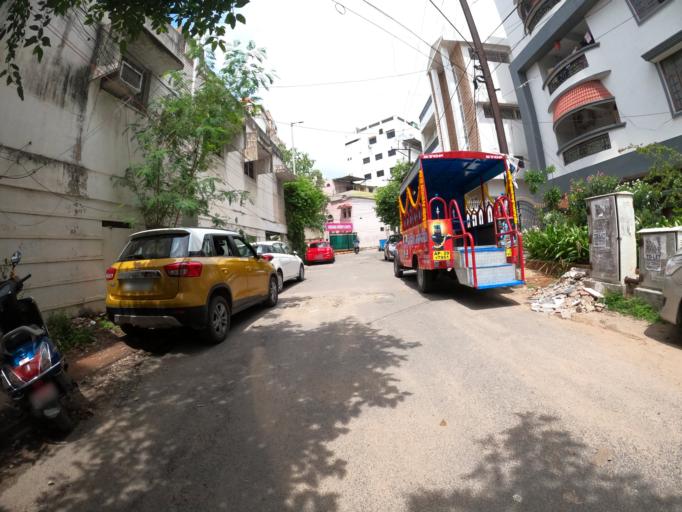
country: IN
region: Telangana
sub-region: Hyderabad
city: Hyderabad
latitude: 17.3994
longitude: 78.4852
